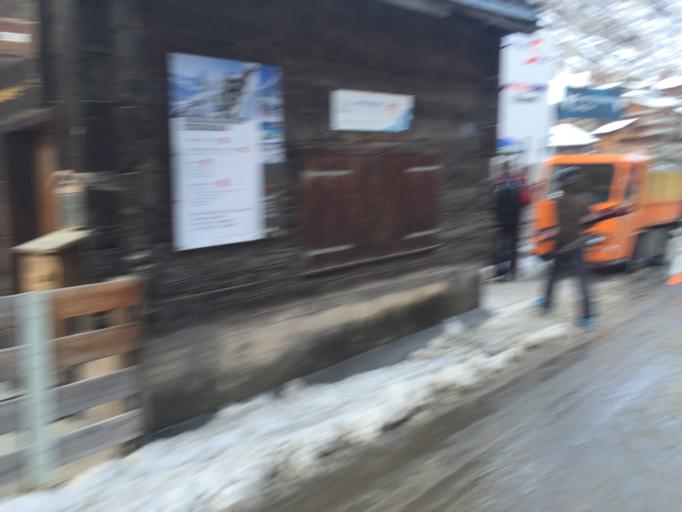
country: CH
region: Valais
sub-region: Visp District
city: Zermatt
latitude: 46.0150
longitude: 7.7427
